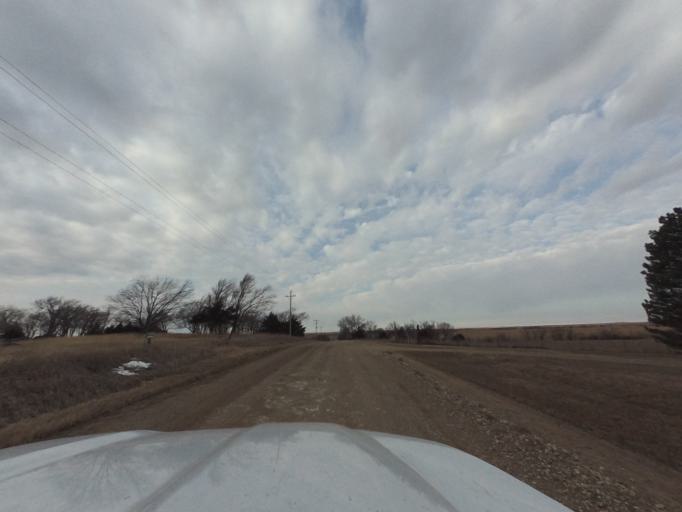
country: US
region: Kansas
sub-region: Chase County
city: Cottonwood Falls
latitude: 38.4492
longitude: -96.3712
